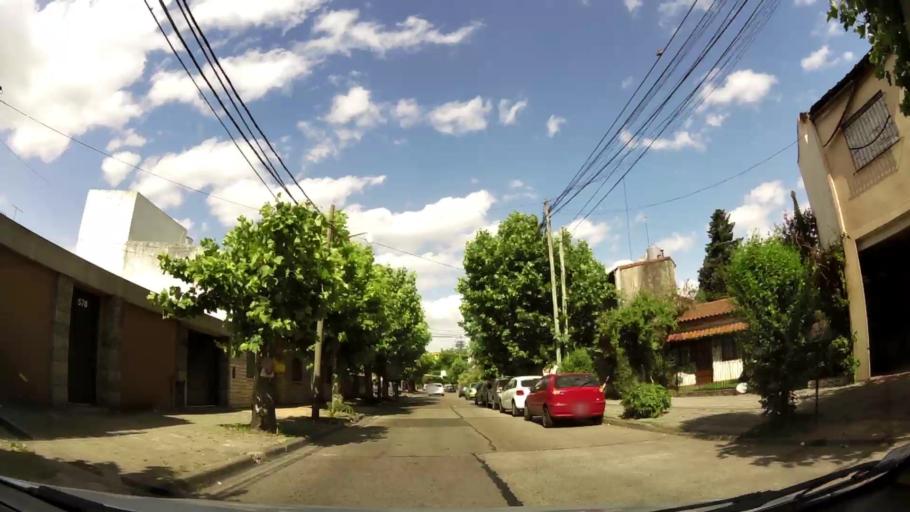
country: AR
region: Buenos Aires
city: San Justo
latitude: -34.6410
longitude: -58.5555
